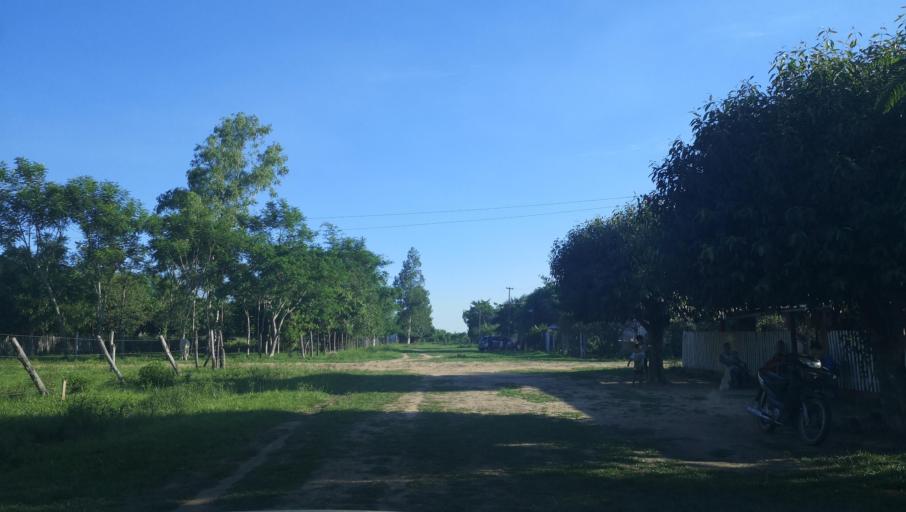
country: PY
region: Caaguazu
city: Carayao
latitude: -25.1996
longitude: -56.4031
